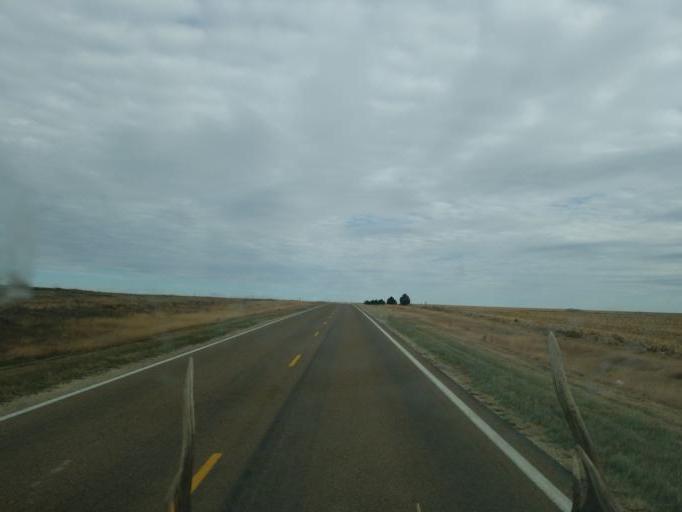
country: US
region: Kansas
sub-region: Wallace County
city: Sharon Springs
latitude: 39.0244
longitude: -101.3252
